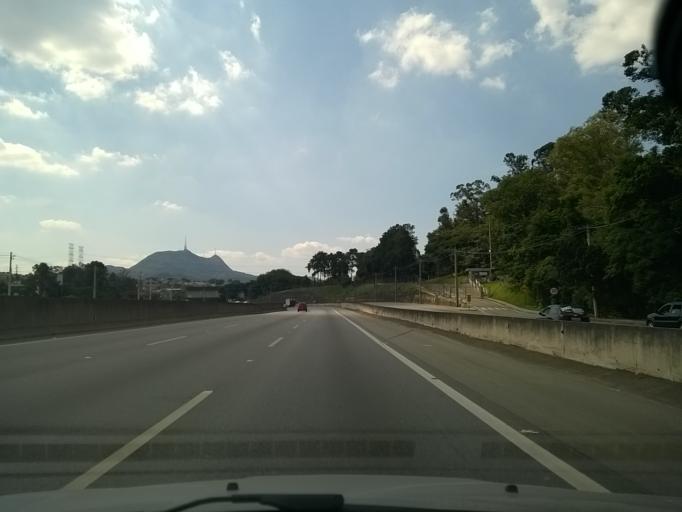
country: BR
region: Sao Paulo
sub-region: Osasco
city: Osasco
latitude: -23.4961
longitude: -46.7549
